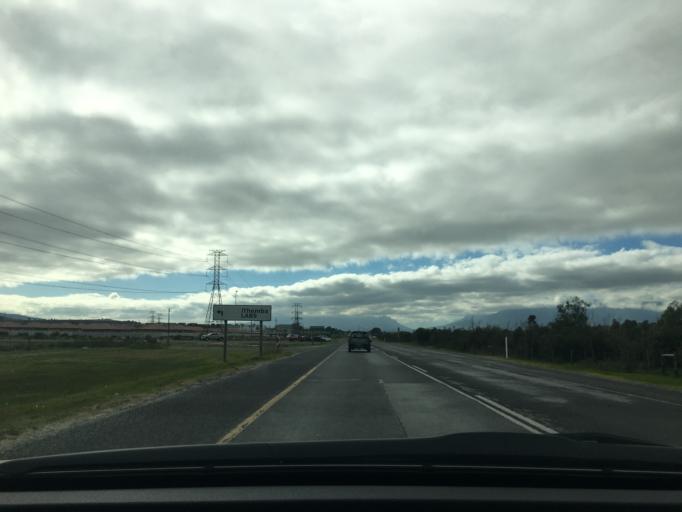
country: ZA
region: Western Cape
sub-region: Cape Winelands District Municipality
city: Stellenbosch
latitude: -34.0265
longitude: 18.7354
